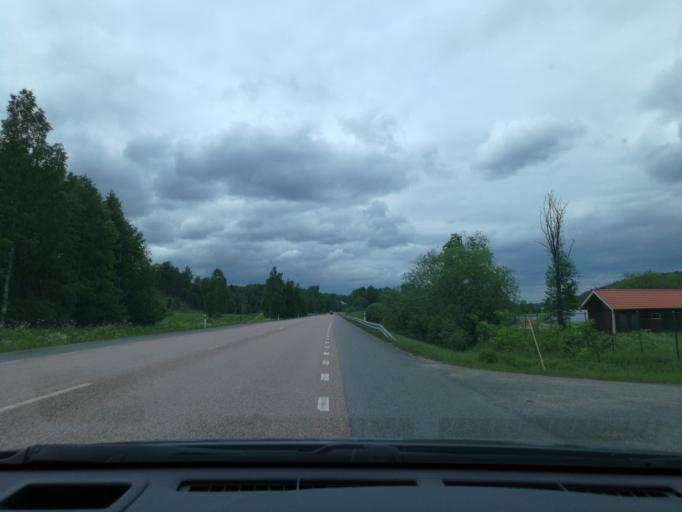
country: SE
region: Vaestmanland
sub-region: Fagersta Kommun
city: Fagersta
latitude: 59.9834
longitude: 15.6855
